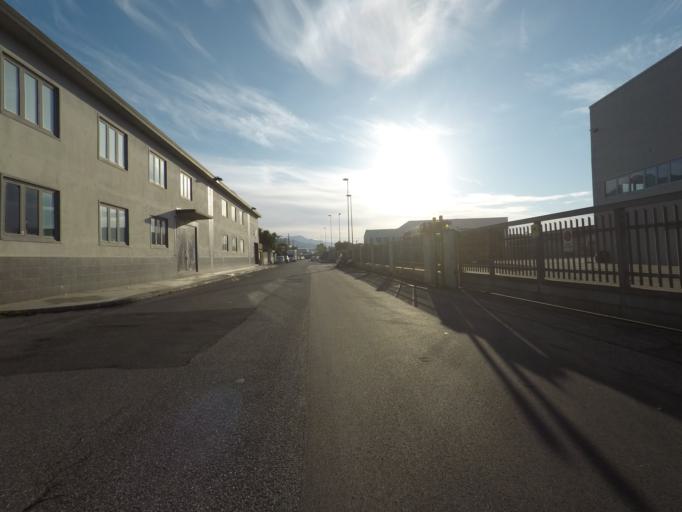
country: IT
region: Tuscany
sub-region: Provincia di Massa-Carrara
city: Massa
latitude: 44.0297
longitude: 10.1104
